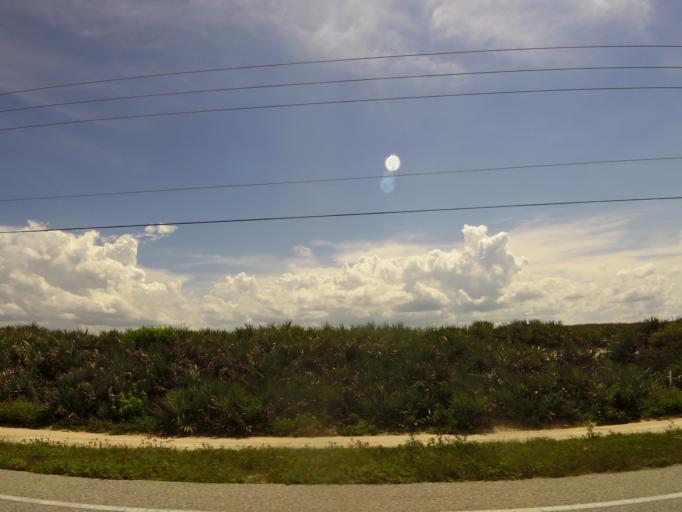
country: US
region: Florida
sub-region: Volusia County
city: Ormond-by-the-Sea
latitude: 29.4048
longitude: -81.0924
